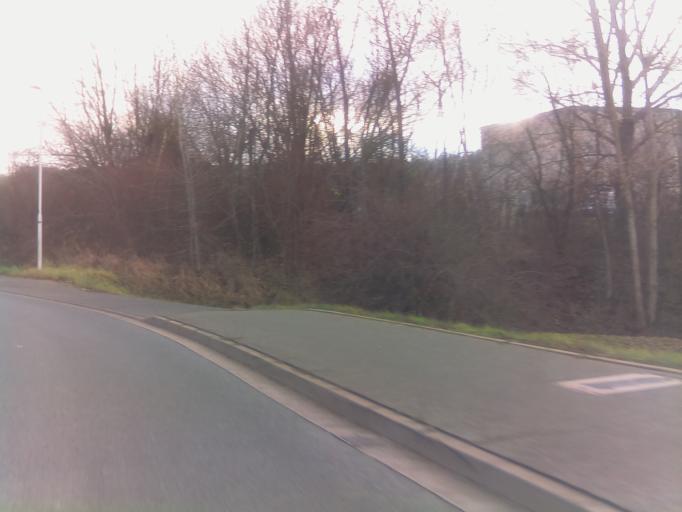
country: DE
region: Thuringia
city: Unterwellenborn
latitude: 50.6513
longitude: 11.4348
